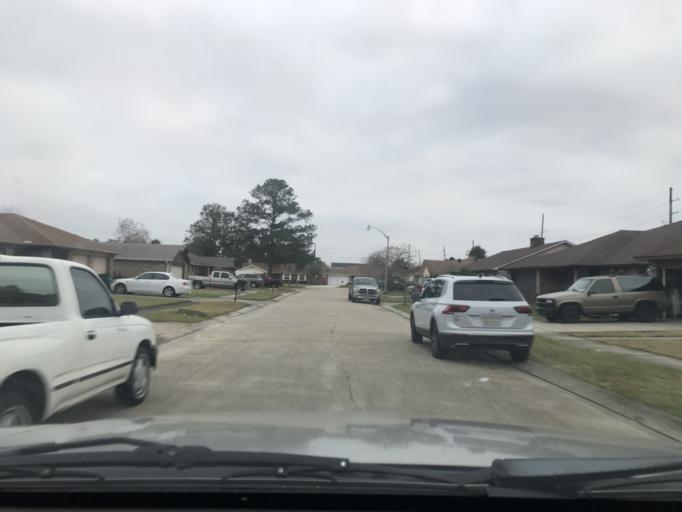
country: US
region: Louisiana
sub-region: Jefferson Parish
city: Woodmere
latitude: 29.8607
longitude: -90.0806
